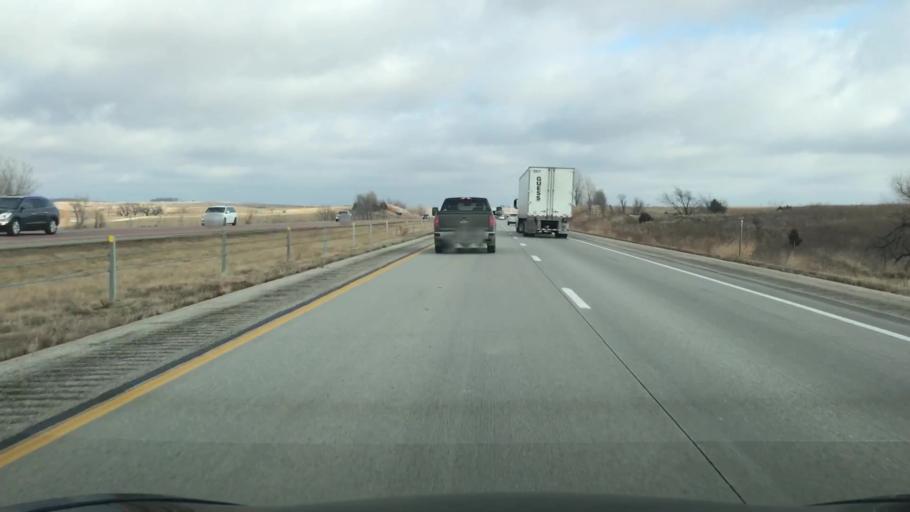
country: US
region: Iowa
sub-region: Guthrie County
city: Guthrie Center
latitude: 41.4935
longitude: -94.5960
